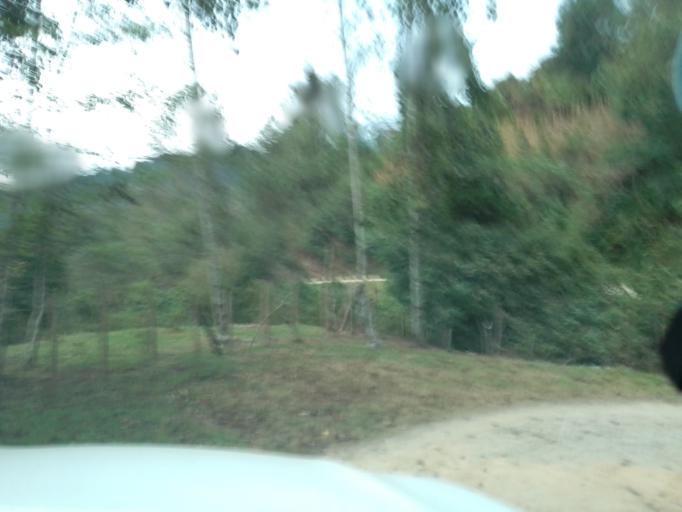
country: MX
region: Chiapas
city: Motozintla de Mendoza
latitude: 15.2163
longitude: -92.2297
